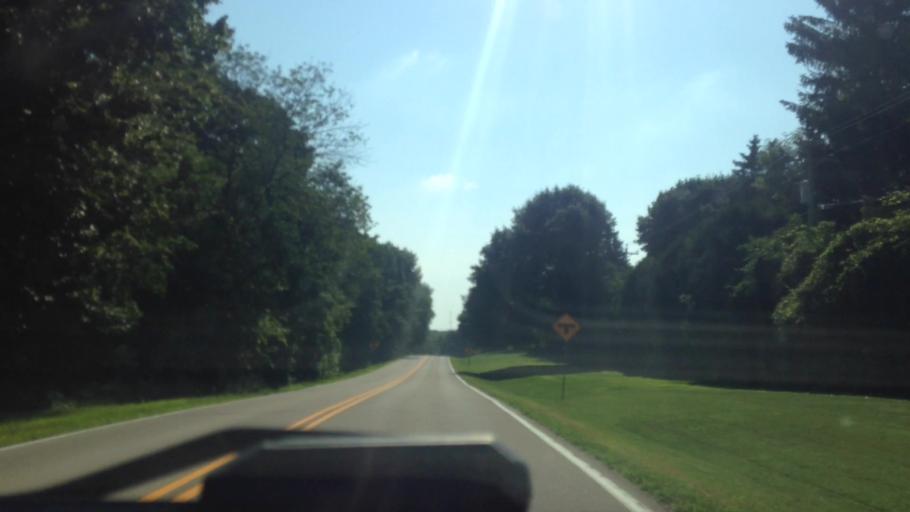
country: US
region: Wisconsin
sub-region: Waukesha County
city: Lannon
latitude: 43.1627
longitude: -88.1872
